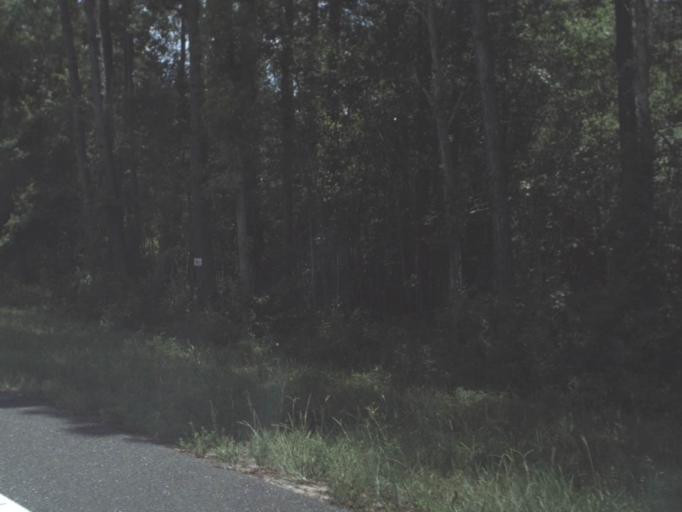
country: US
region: Florida
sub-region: Taylor County
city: Perry
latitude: 30.1933
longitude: -83.6486
